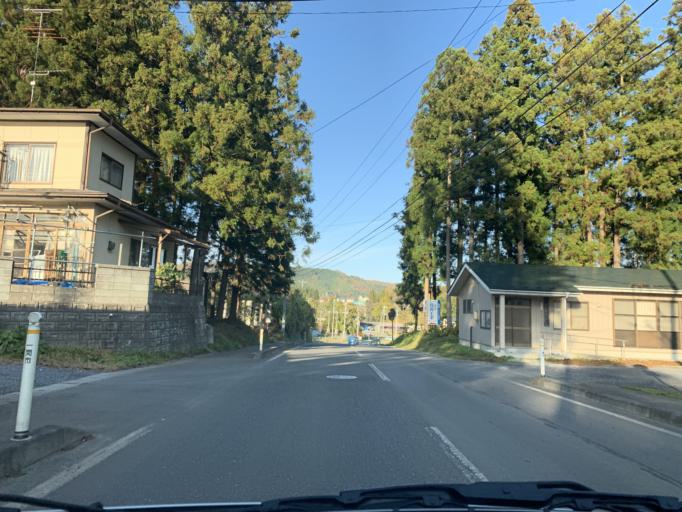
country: JP
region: Iwate
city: Ichinoseki
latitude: 38.9313
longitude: 141.0810
